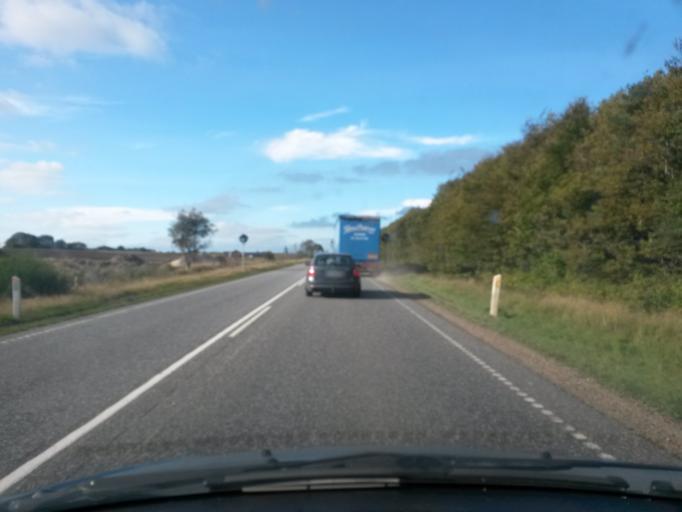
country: DK
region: Central Jutland
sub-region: Herning Kommune
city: Avlum
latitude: 56.2955
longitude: 8.7247
